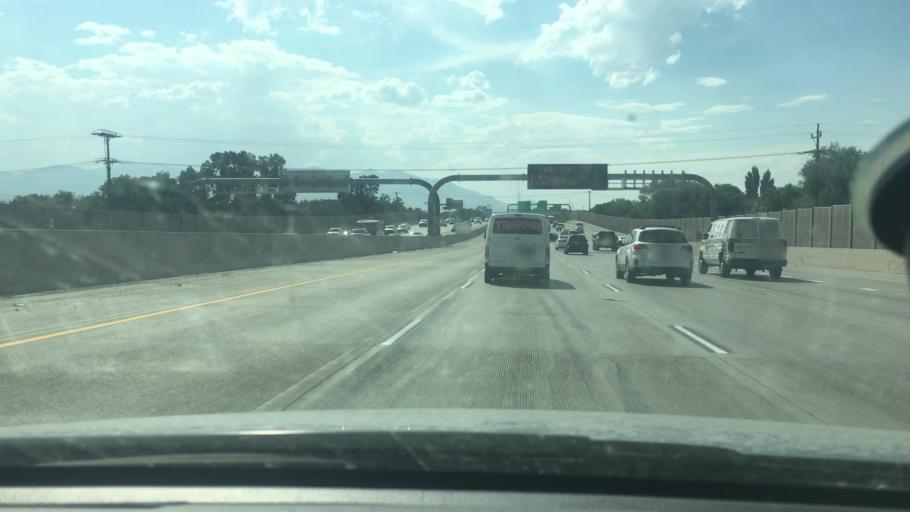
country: US
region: Utah
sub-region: Salt Lake County
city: South Salt Lake
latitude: 40.7167
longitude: -111.8770
